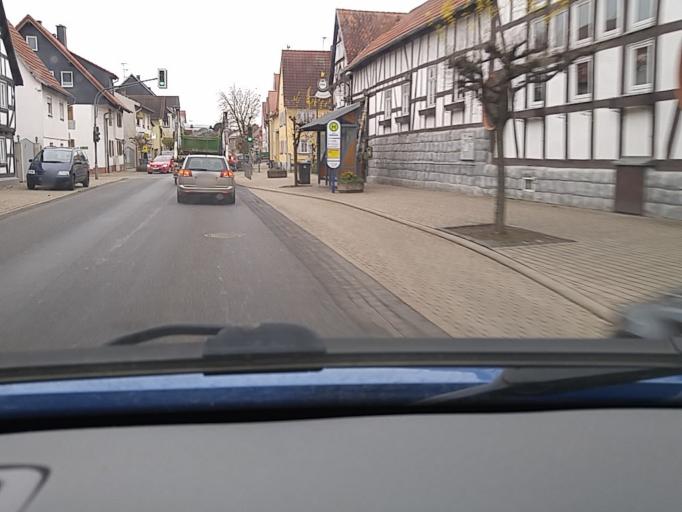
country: DE
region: Hesse
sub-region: Regierungsbezirk Darmstadt
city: Echzell
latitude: 50.3916
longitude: 8.8866
